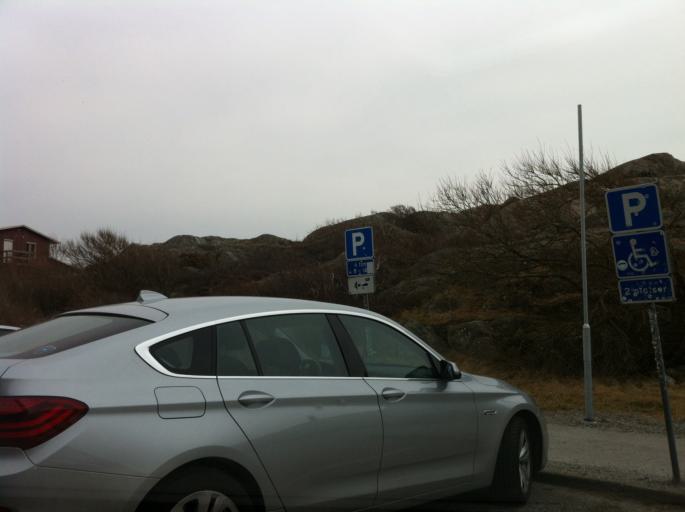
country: SE
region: Vaestra Goetaland
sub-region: Tjorns Kommun
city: Myggenas
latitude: 58.1453
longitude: 11.7081
